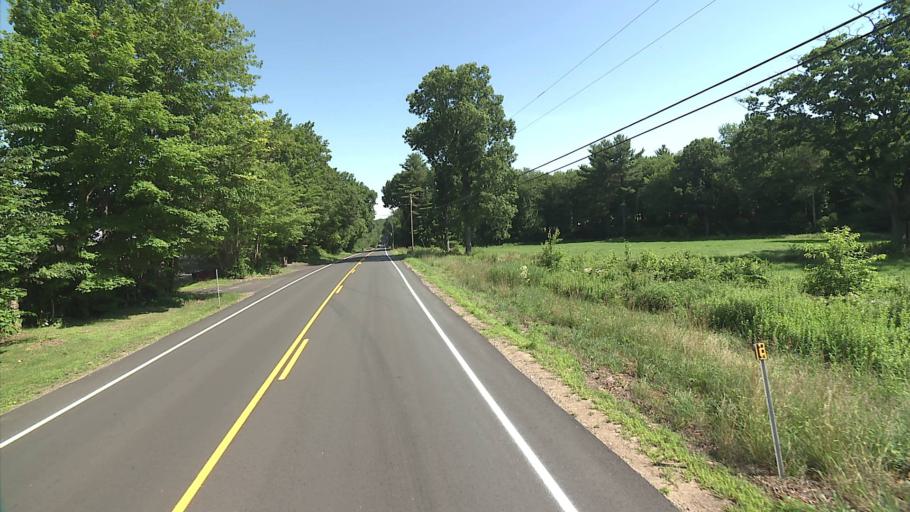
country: US
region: Connecticut
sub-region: Litchfield County
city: Northwest Harwinton
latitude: 41.7599
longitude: -73.0248
